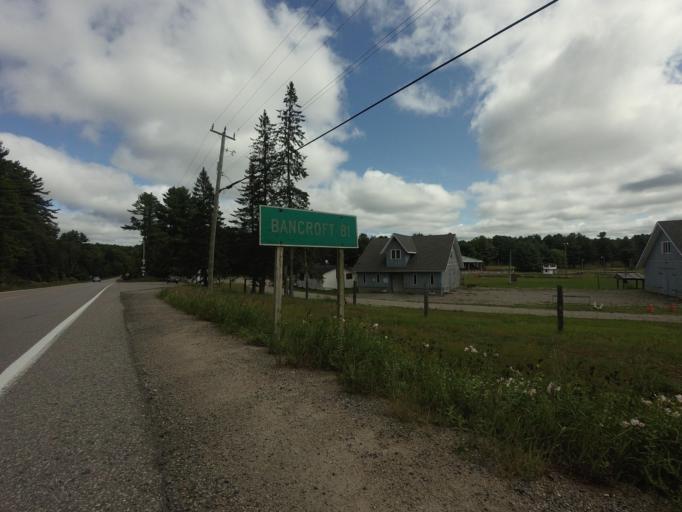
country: CA
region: Ontario
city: Omemee
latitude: 44.7839
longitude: -78.6464
